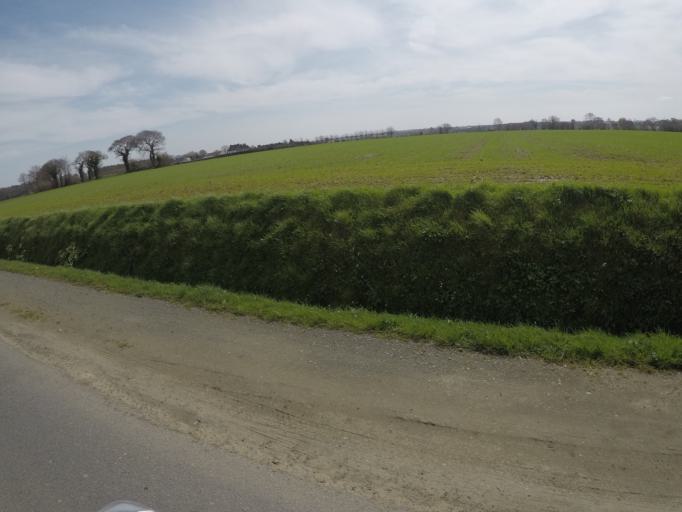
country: FR
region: Brittany
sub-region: Departement des Cotes-d'Armor
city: Plelo
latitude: 48.5597
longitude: -2.9392
